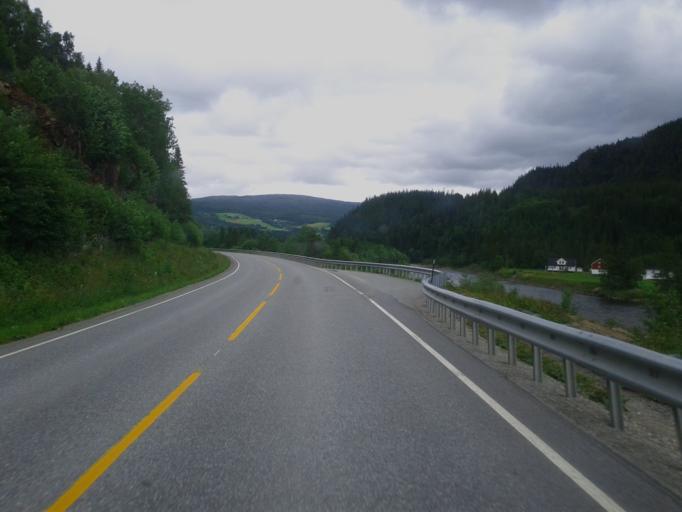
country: NO
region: Sor-Trondelag
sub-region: Midtre Gauldal
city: Storen
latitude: 62.9436
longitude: 10.6750
